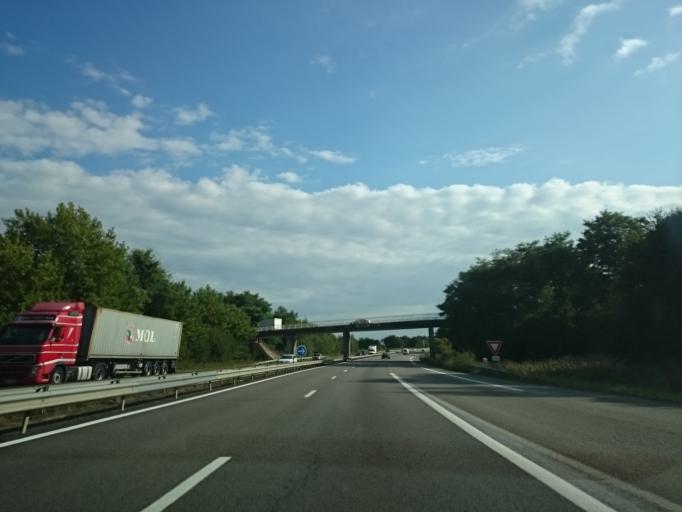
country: FR
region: Pays de la Loire
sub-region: Departement de la Loire-Atlantique
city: Heric
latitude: 47.3775
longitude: -1.6426
